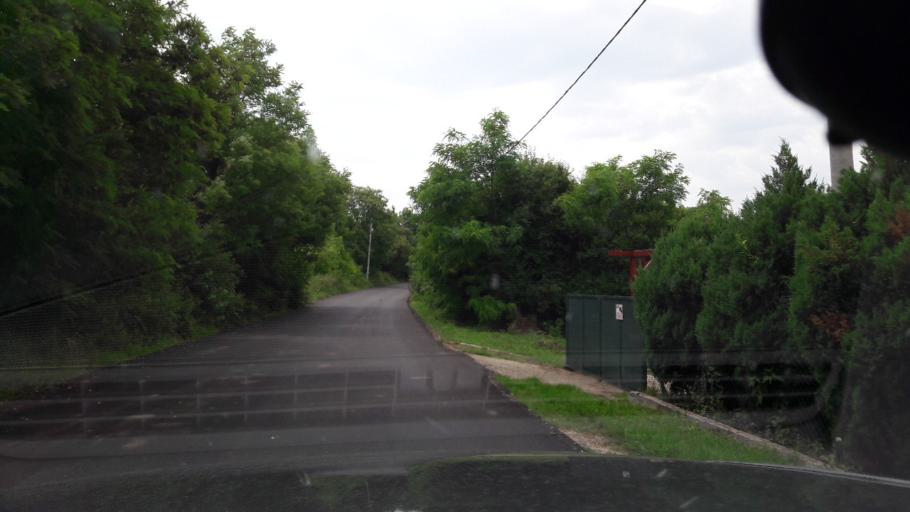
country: RS
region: Central Serbia
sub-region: Belgrade
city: Sopot
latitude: 44.6062
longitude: 20.6012
